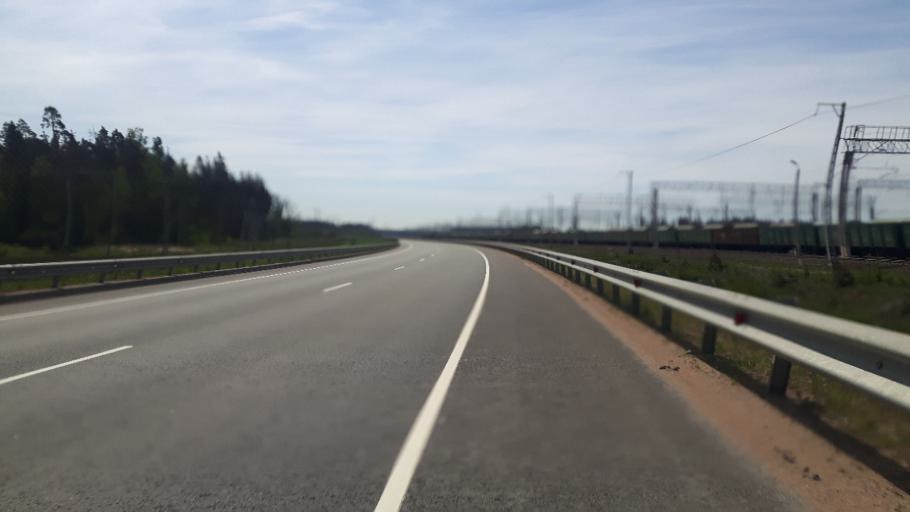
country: RU
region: Leningrad
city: Vistino
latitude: 59.6710
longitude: 28.4328
